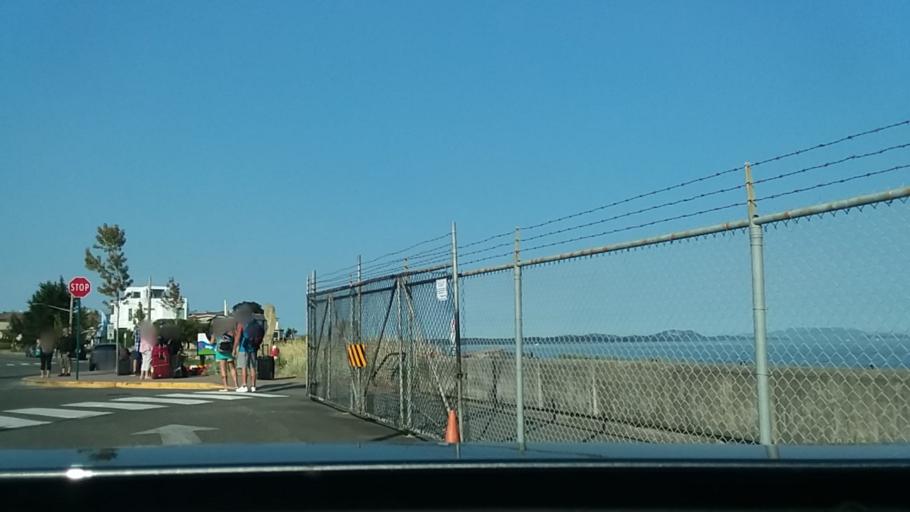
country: CA
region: British Columbia
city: North Saanich
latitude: 48.6443
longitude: -123.3968
